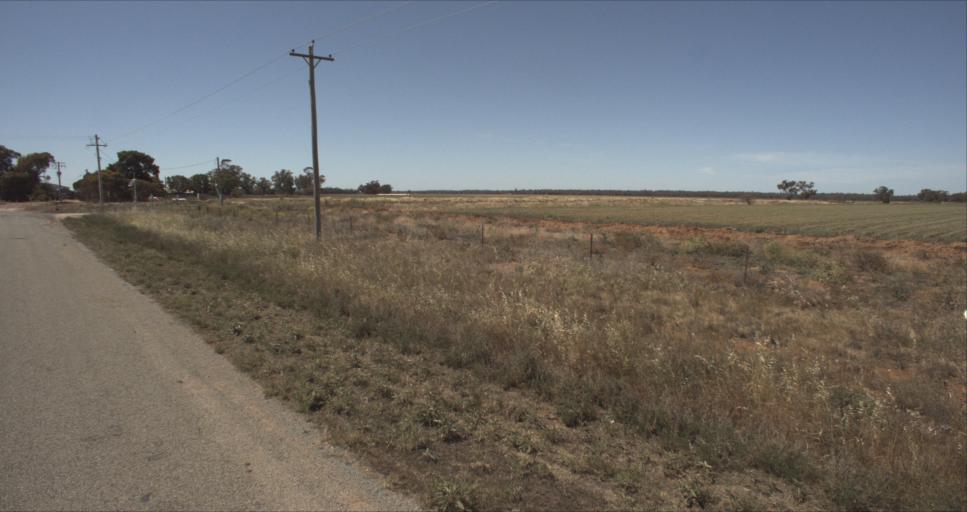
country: AU
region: New South Wales
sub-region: Leeton
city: Leeton
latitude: -34.5833
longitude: 146.3074
